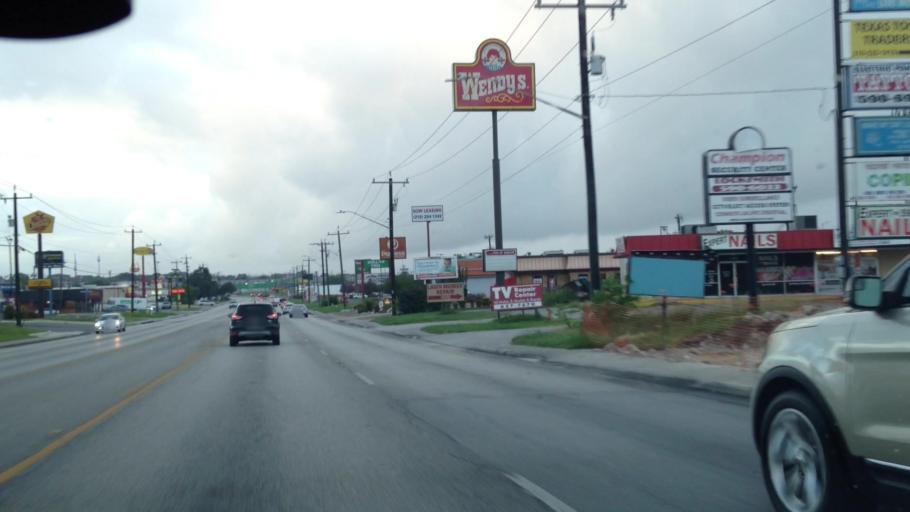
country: US
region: Texas
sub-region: Bexar County
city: Windcrest
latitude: 29.5495
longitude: -98.4082
